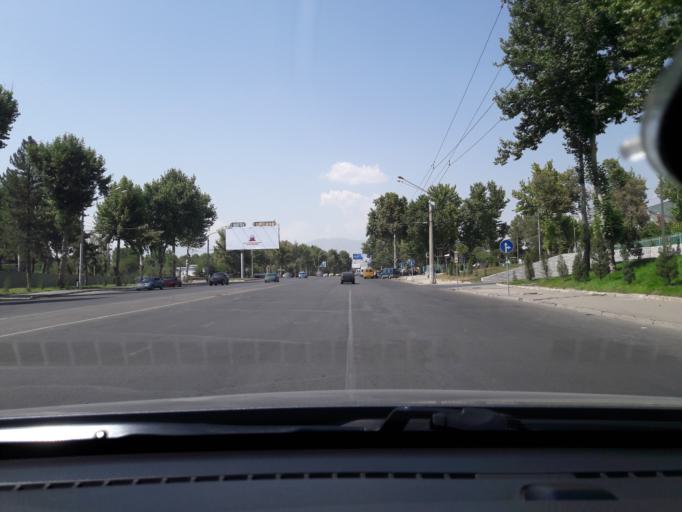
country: TJ
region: Dushanbe
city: Dushanbe
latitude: 38.5702
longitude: 68.7548
